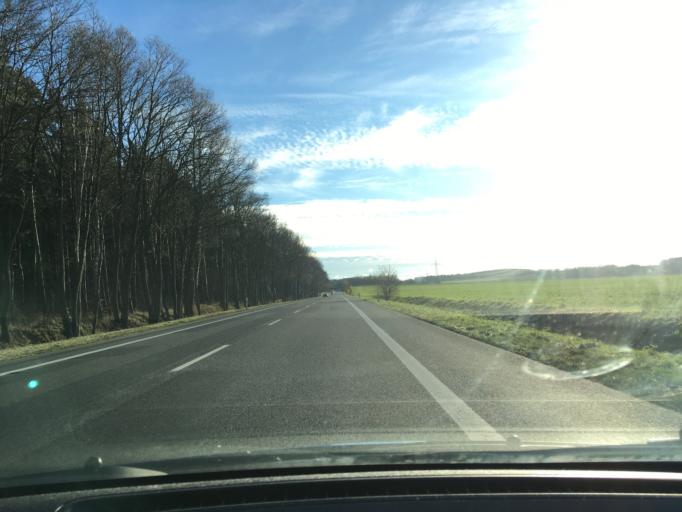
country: DE
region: Lower Saxony
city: Jelmstorf
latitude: 53.0873
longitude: 10.5277
